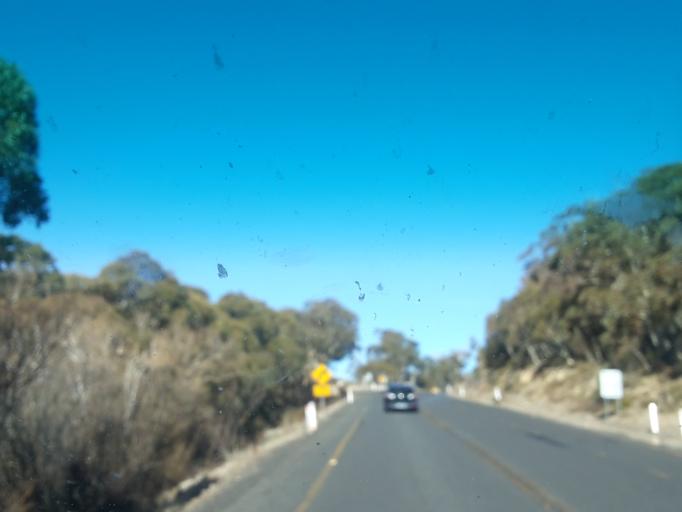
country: AU
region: New South Wales
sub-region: Snowy River
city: Jindabyne
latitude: -36.4550
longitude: 148.4722
